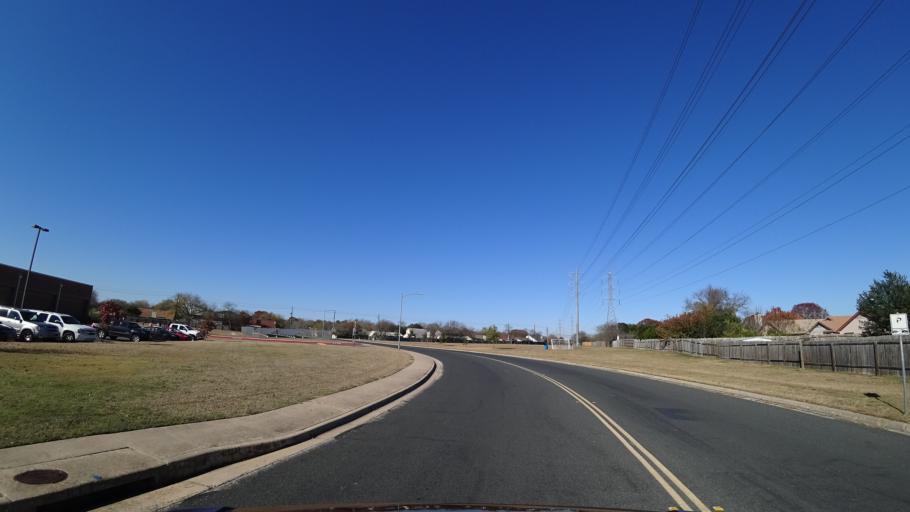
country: US
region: Texas
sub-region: Travis County
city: Wells Branch
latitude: 30.4173
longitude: -97.6887
